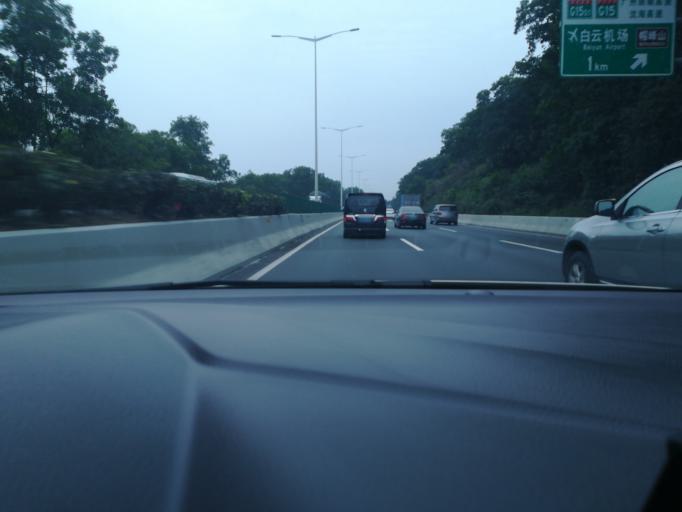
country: CN
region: Guangdong
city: Taihe
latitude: 23.2653
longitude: 113.3599
